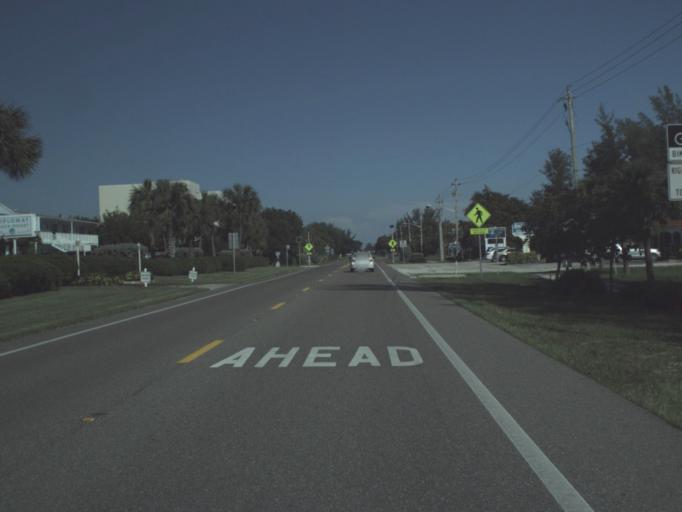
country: US
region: Florida
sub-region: Manatee County
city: Longboat Key
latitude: 27.3726
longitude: -82.6305
